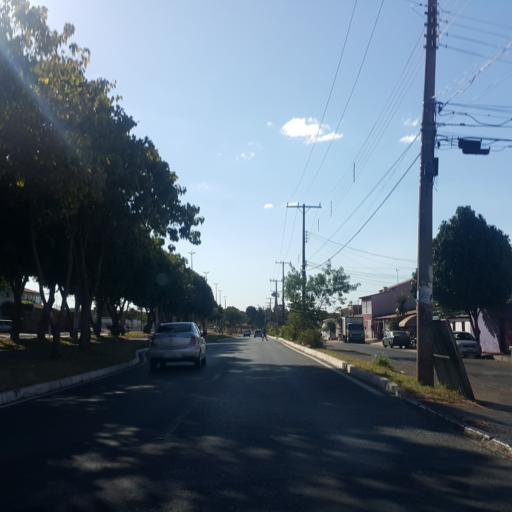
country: BR
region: Federal District
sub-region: Brasilia
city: Brasilia
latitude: -15.7971
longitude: -48.1103
